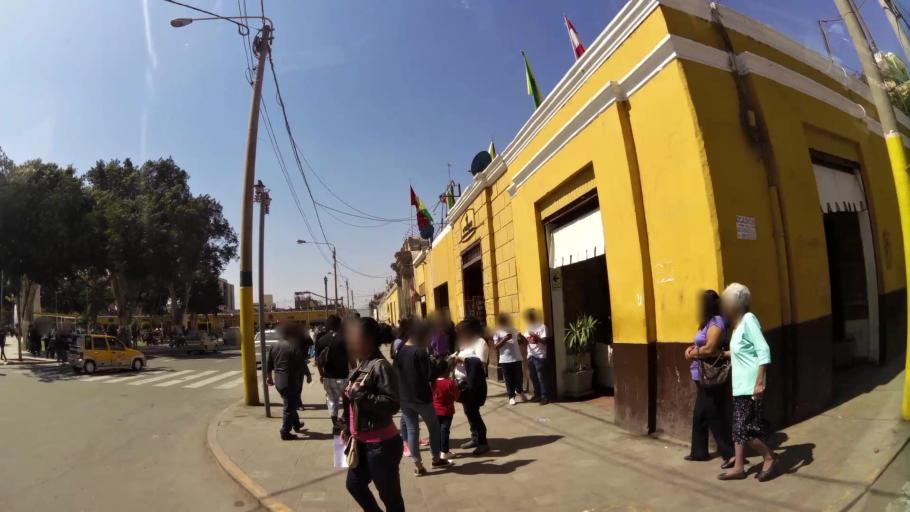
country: PE
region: Ica
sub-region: Provincia de Ica
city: Ica
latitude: -14.0646
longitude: -75.7294
